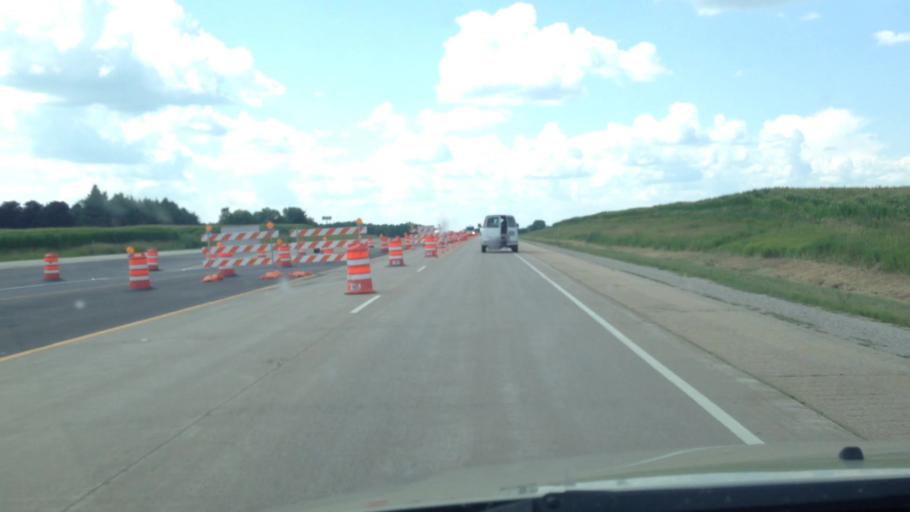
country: US
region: Wisconsin
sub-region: Brown County
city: Pulaski
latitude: 44.6909
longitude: -88.3298
